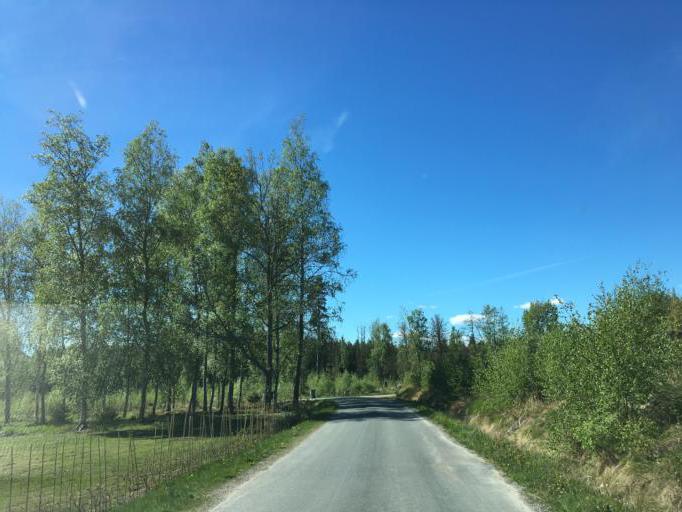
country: SE
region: Soedermanland
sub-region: Eskilstuna Kommun
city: Hallbybrunn
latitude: 59.3537
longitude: 16.3678
